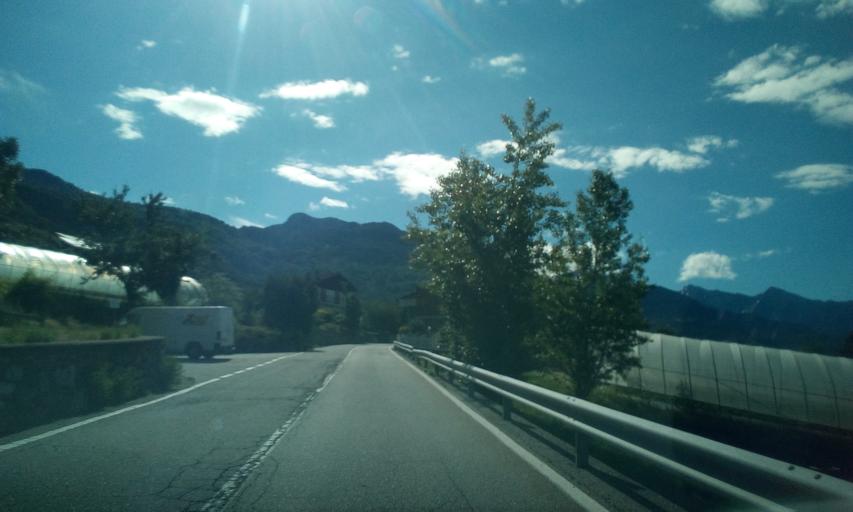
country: IT
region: Aosta Valley
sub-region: Valle d'Aosta
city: Saint-Vincent
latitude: 45.7549
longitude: 7.6407
